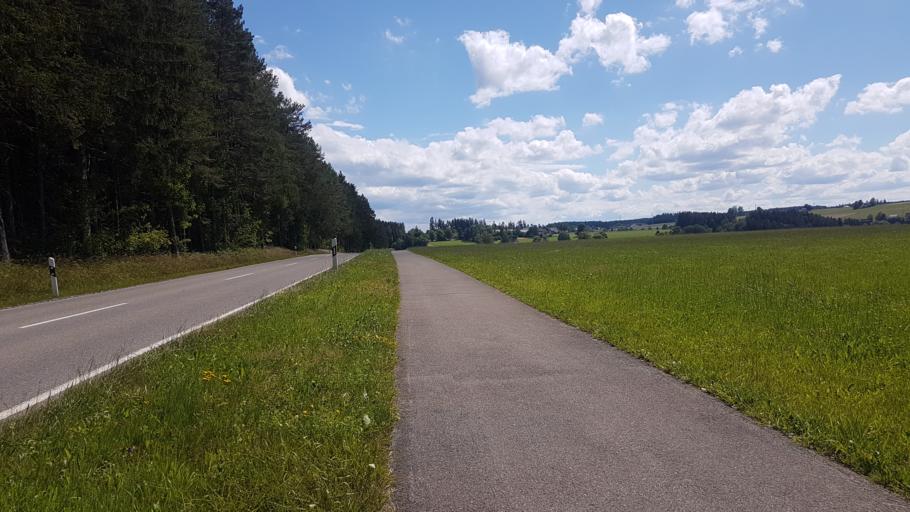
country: DE
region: Baden-Wuerttemberg
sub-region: Freiburg Region
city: Hardt
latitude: 48.1994
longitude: 8.4136
